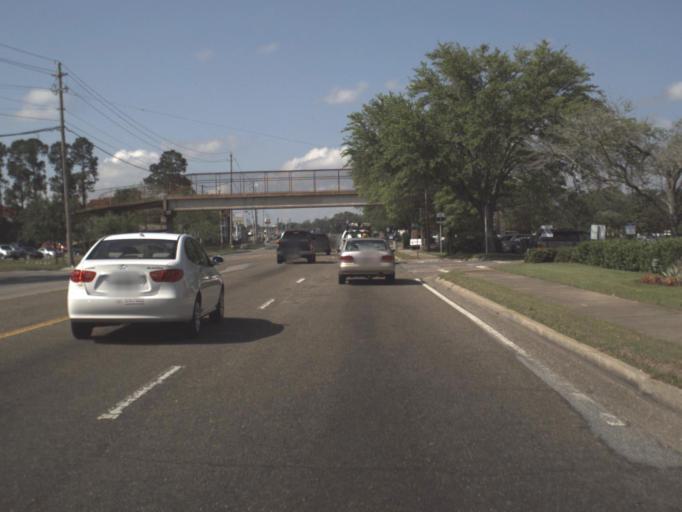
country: US
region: Florida
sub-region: Escambia County
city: Ferry Pass
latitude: 30.5154
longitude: -87.2169
